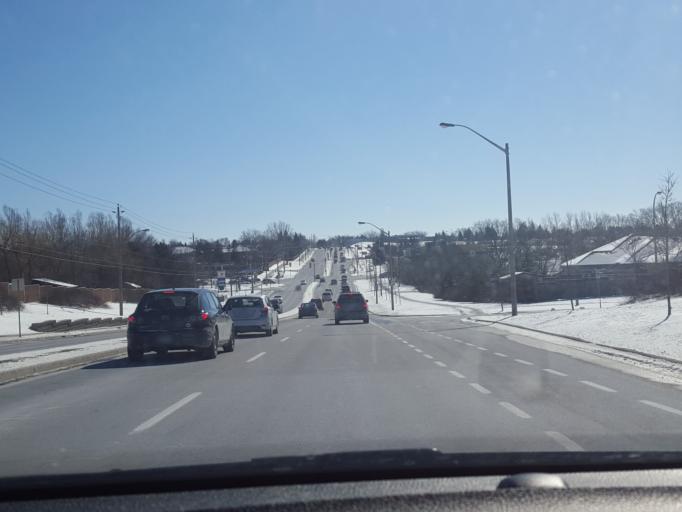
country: CA
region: Ontario
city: Kitchener
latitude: 43.4343
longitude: -80.5273
